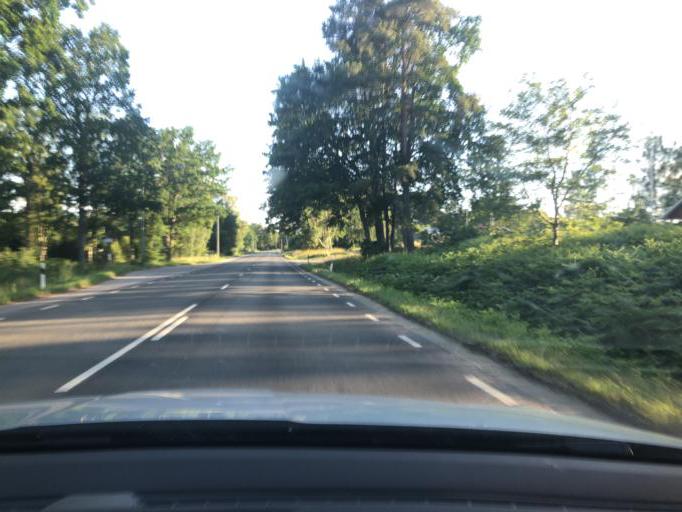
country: SE
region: Blekinge
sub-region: Karlshamns Kommun
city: Morrum
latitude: 56.1518
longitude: 14.6718
